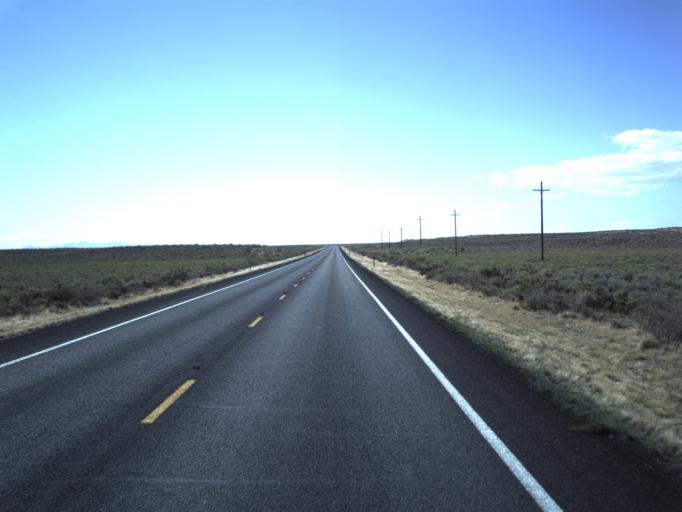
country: US
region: Utah
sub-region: Beaver County
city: Milford
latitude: 38.4539
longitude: -113.0064
